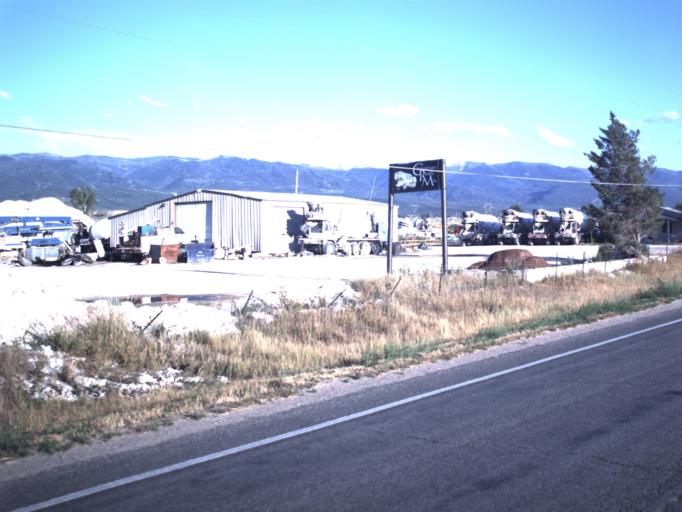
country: US
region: Utah
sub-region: Sanpete County
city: Mount Pleasant
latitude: 39.5749
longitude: -111.4554
